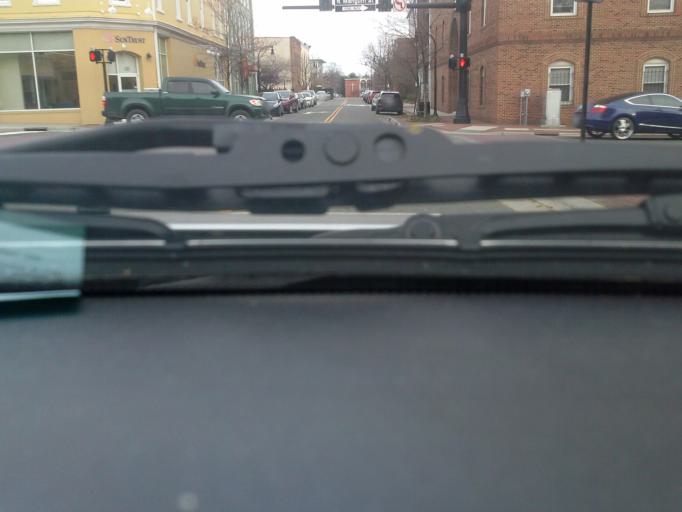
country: US
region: North Carolina
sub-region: Durham County
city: Durham
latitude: 35.9957
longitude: -78.9004
